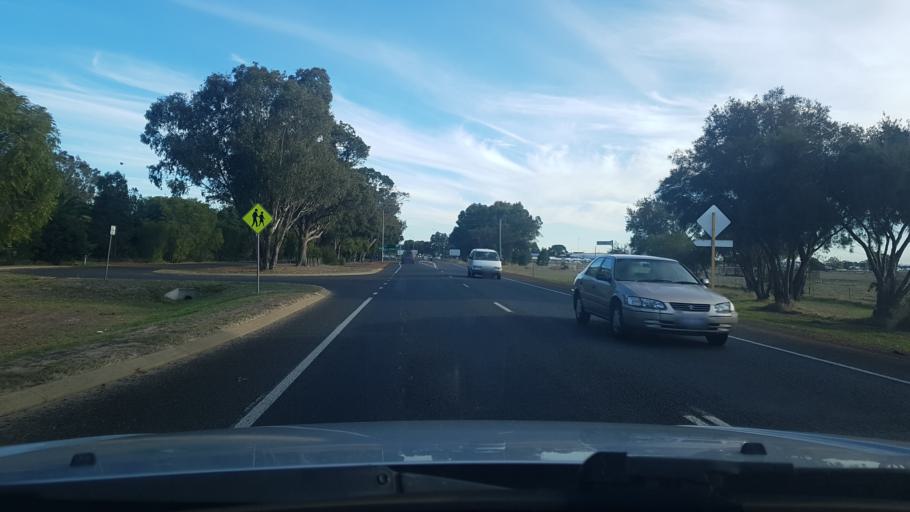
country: AU
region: Western Australia
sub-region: Busselton
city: Vasse
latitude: -33.6717
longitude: 115.2559
